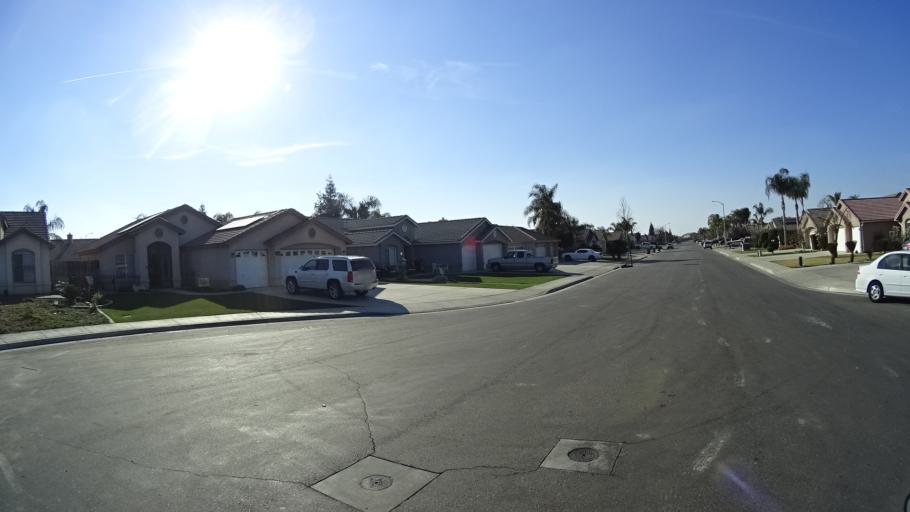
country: US
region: California
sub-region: Kern County
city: Greenfield
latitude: 35.2864
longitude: -119.0524
